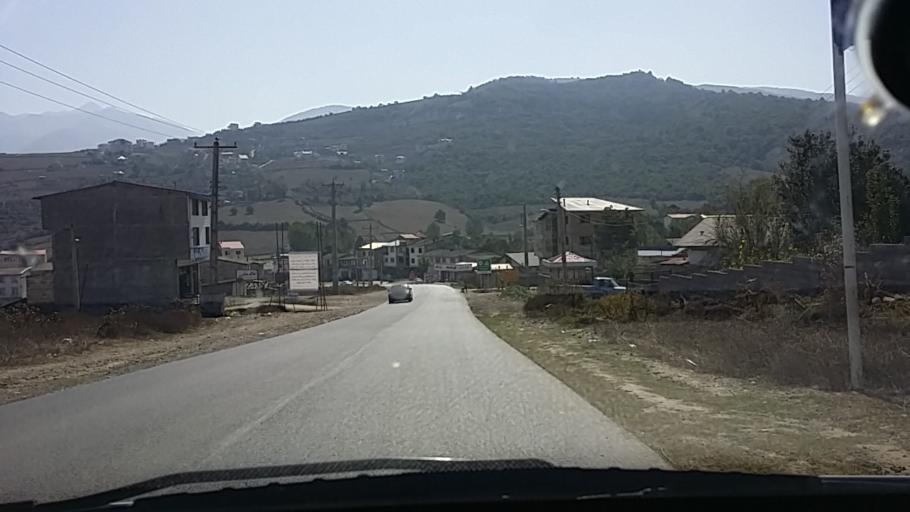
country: IR
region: Mazandaran
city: `Abbasabad
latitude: 36.5485
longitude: 51.1709
